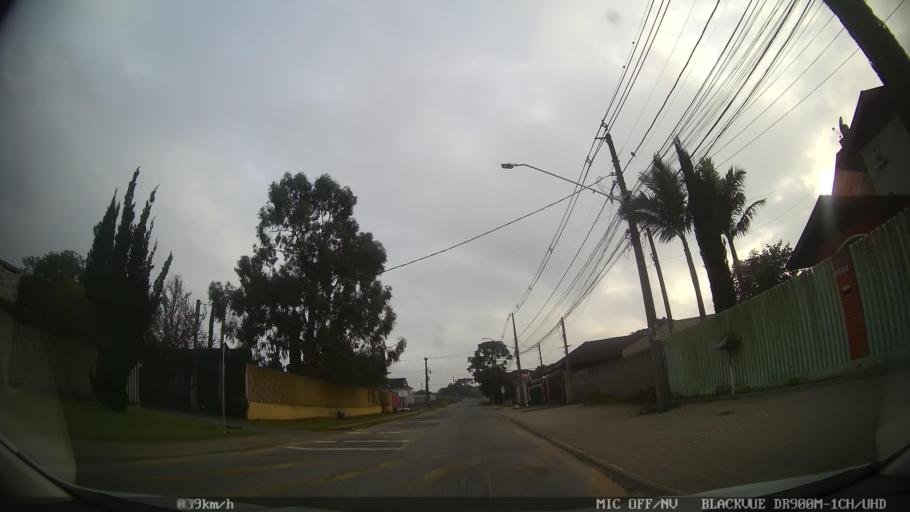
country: BR
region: Parana
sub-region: Almirante Tamandare
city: Almirante Tamandare
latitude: -25.3847
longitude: -49.3384
